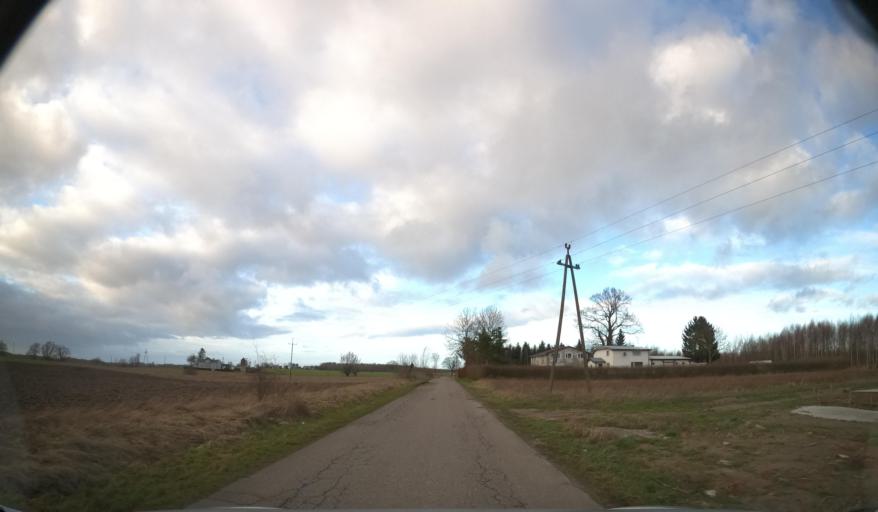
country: PL
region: West Pomeranian Voivodeship
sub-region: Powiat koszalinski
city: Mielno
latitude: 54.1693
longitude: 16.0361
